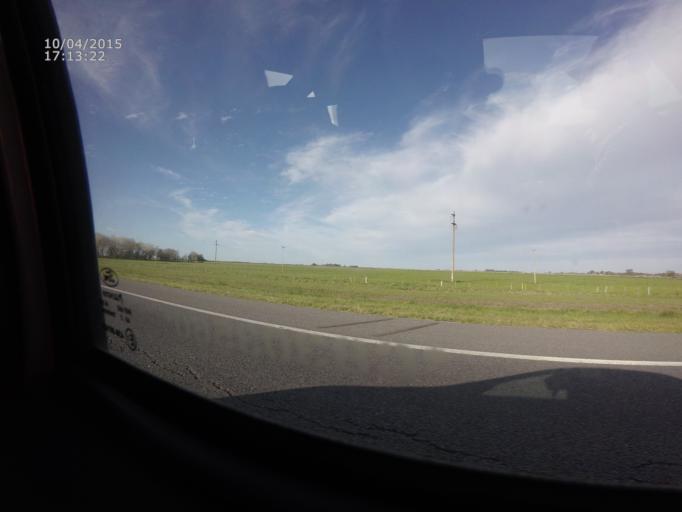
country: AR
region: Buenos Aires
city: Coronel Vidal
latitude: -37.2627
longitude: -57.7816
